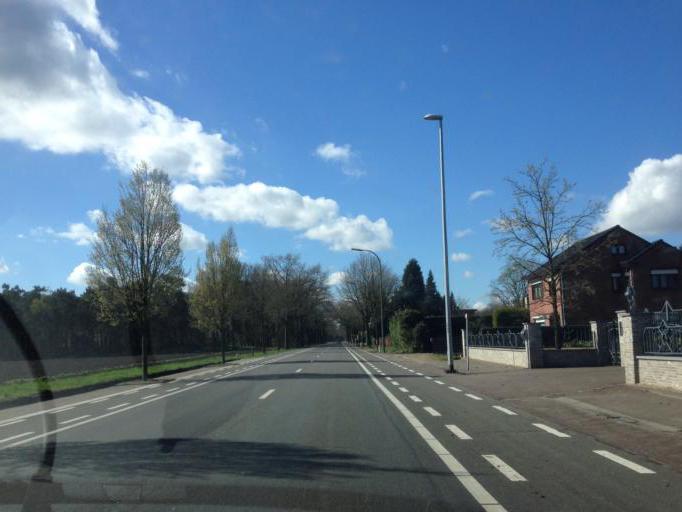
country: BE
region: Flanders
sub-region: Provincie Limburg
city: Overpelt
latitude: 51.2609
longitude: 5.3922
